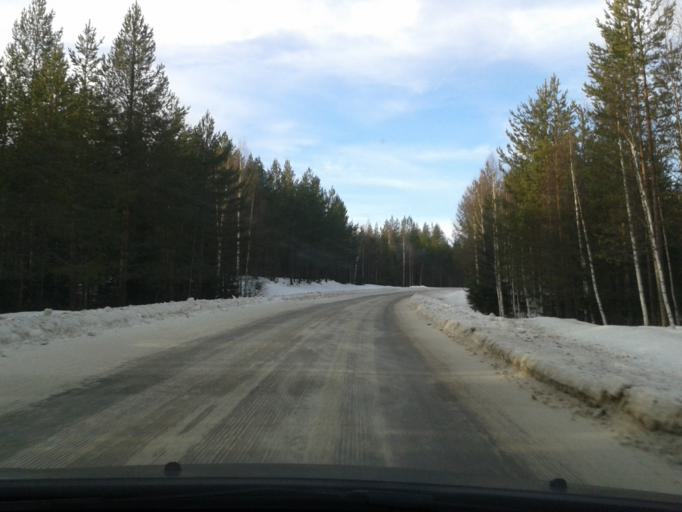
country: SE
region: Vaesternorrland
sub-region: OErnskoeldsviks Kommun
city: Bredbyn
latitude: 63.5313
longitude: 17.9701
